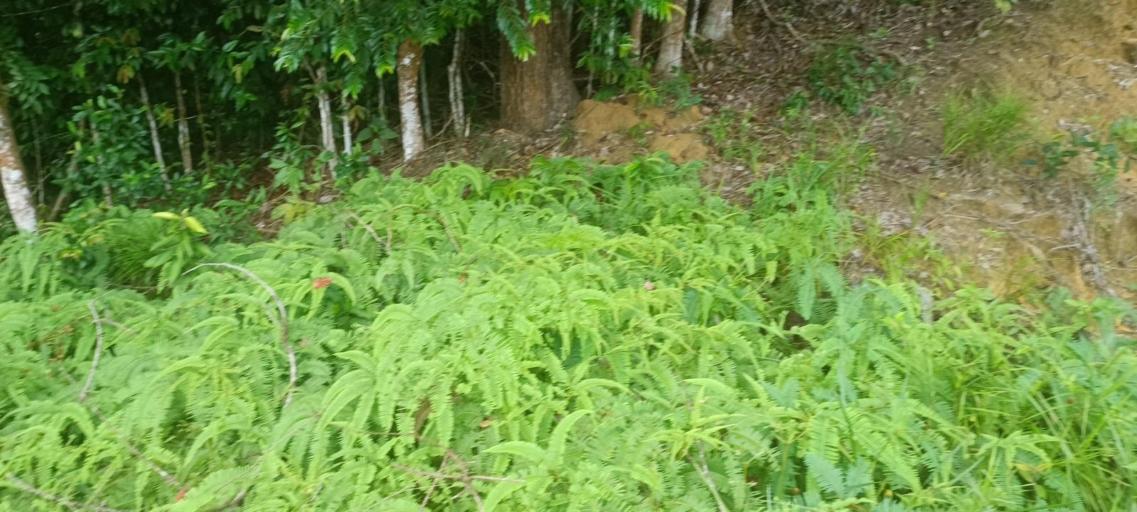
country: MY
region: Penang
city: Bukit Mertajam
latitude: 5.3744
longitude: 100.4986
